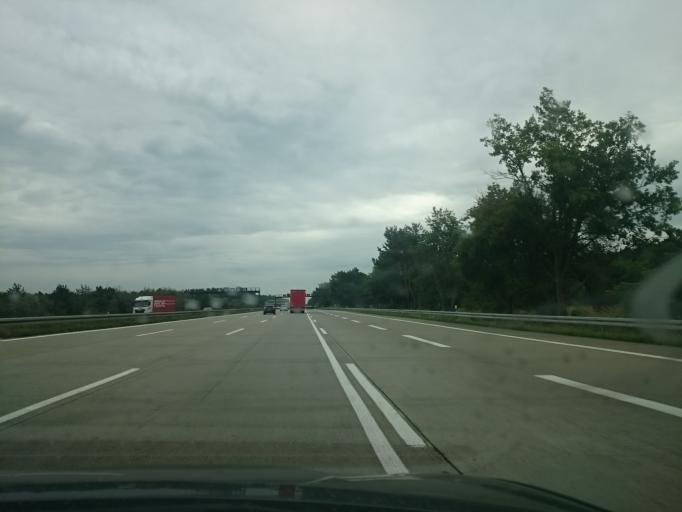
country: DE
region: Brandenburg
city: Fichtenwalde
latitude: 52.3275
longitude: 12.8292
